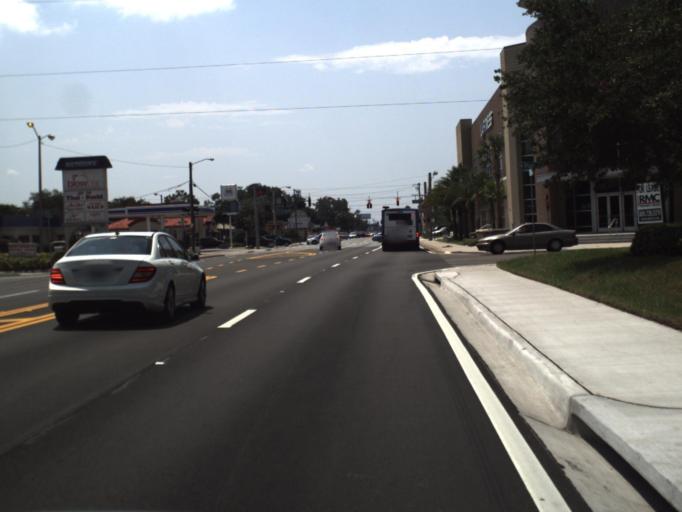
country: US
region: Florida
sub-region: Hillsborough County
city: Tampa
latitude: 27.9425
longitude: -82.5058
